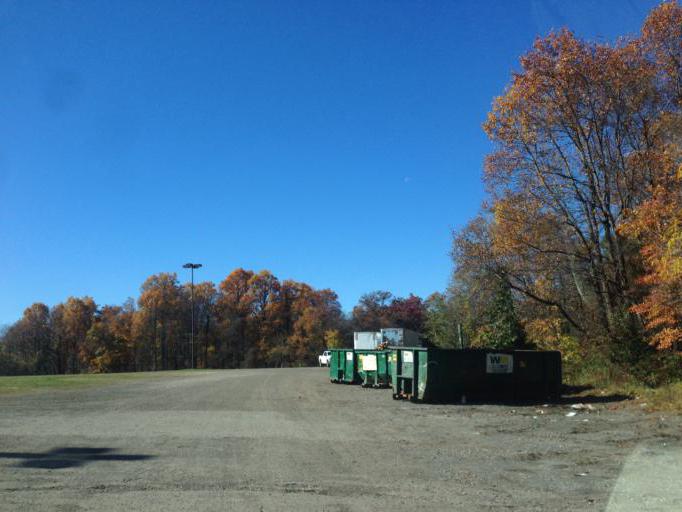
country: US
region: Maryland
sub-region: Howard County
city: Columbia
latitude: 39.2069
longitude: -76.8619
